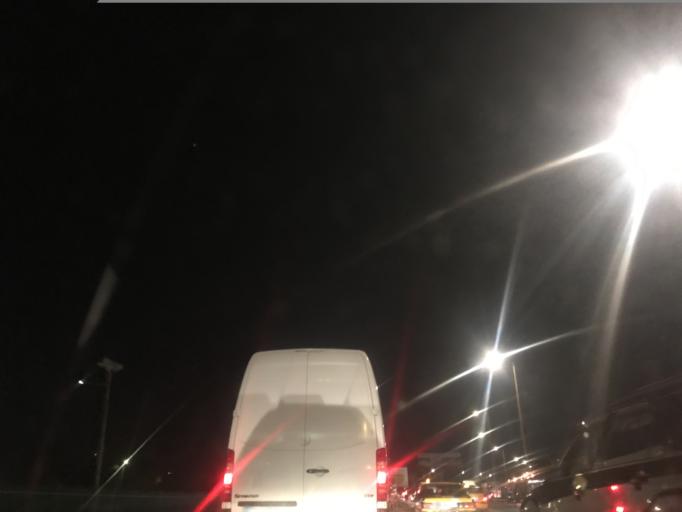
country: SN
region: Dakar
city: Grand Dakar
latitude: 14.7421
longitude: -17.4390
